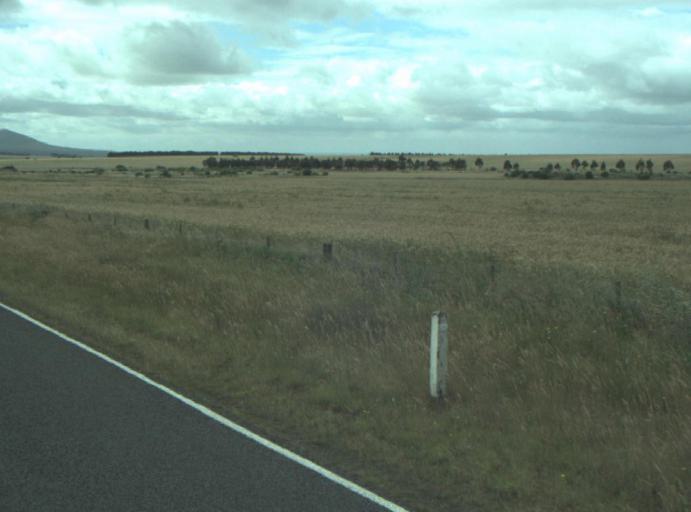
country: AU
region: Victoria
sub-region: Greater Geelong
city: Lara
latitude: -37.8795
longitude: 144.3229
